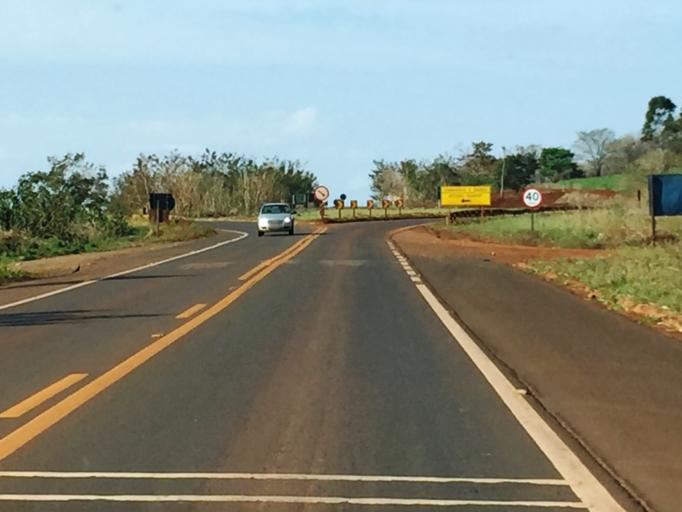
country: BR
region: Sao Paulo
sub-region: Sertaozinho
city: Sertaozinho
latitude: -21.2509
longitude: -47.9769
